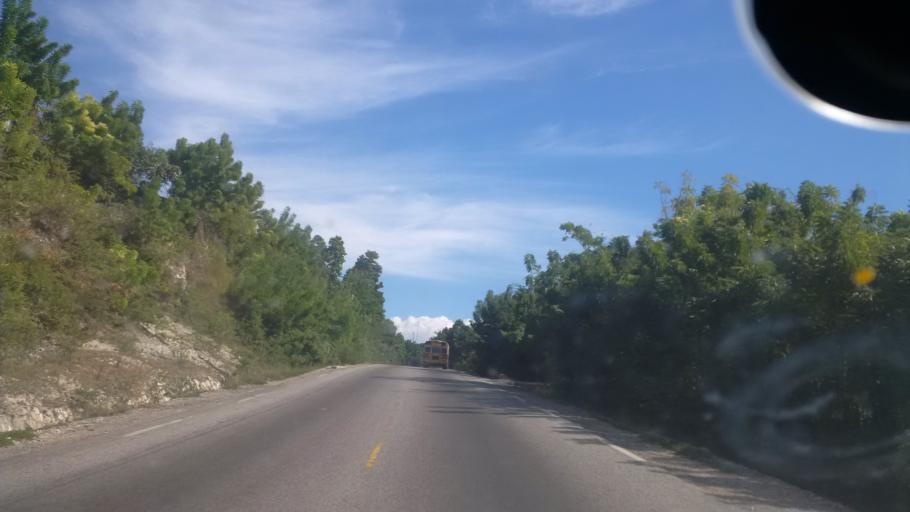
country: HT
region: Ouest
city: Tigwav
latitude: 18.4337
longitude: -72.8245
